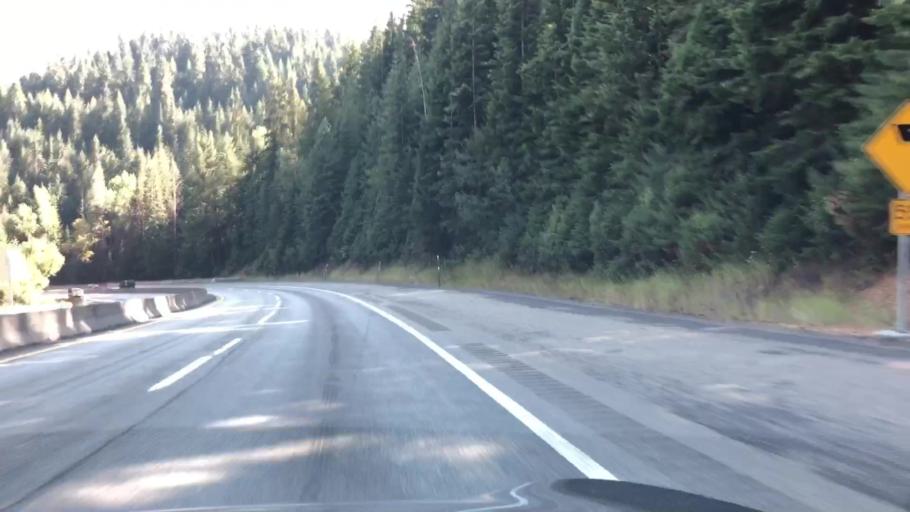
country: US
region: Idaho
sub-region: Kootenai County
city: Coeur d'Alene
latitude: 47.6078
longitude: -116.5117
